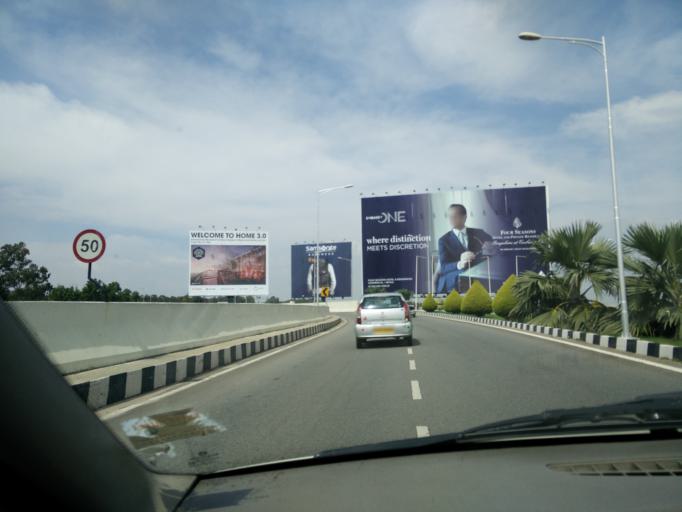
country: IN
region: Karnataka
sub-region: Bangalore Rural
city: Devanhalli
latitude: 13.1996
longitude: 77.6620
